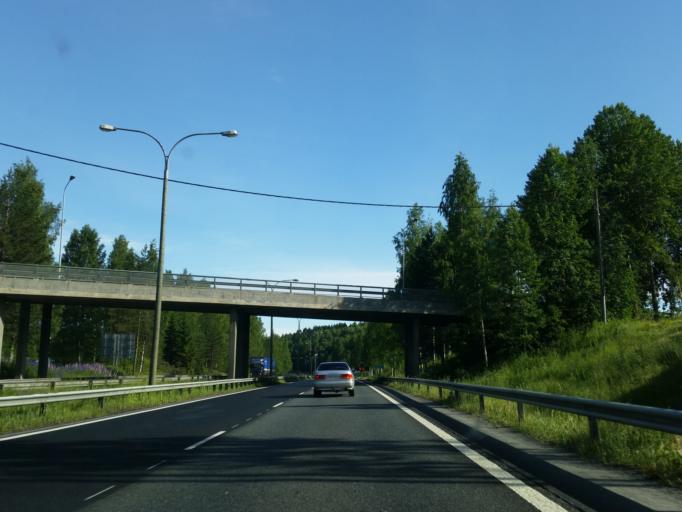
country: FI
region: Northern Savo
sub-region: Kuopio
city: Kuopio
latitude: 62.9211
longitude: 27.6765
